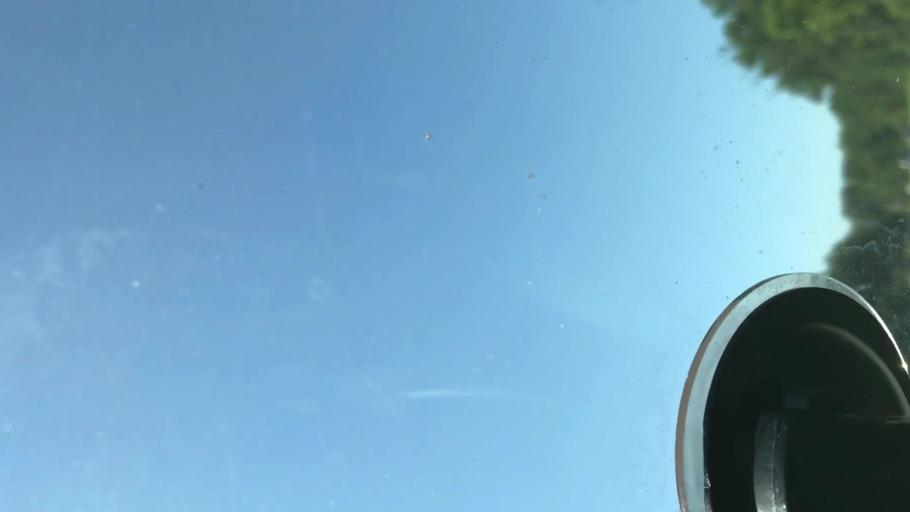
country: US
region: Virginia
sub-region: Spotsylvania County
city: Spotsylvania Courthouse
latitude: 38.1754
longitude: -77.5175
